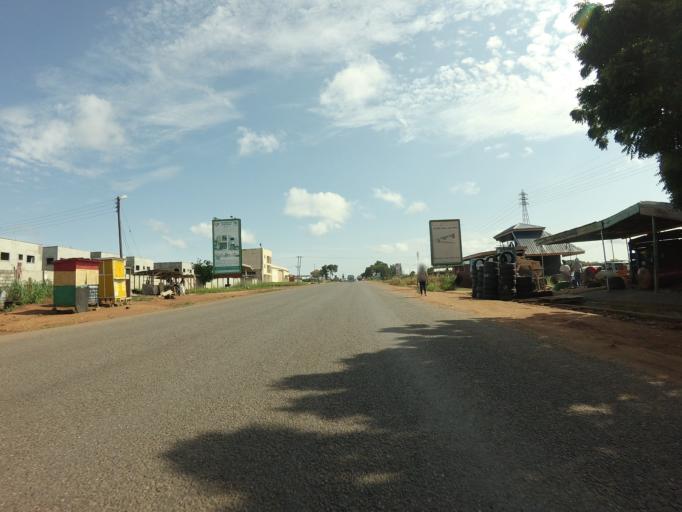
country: GH
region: Eastern
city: Aburi
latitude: 5.7918
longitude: -0.1297
